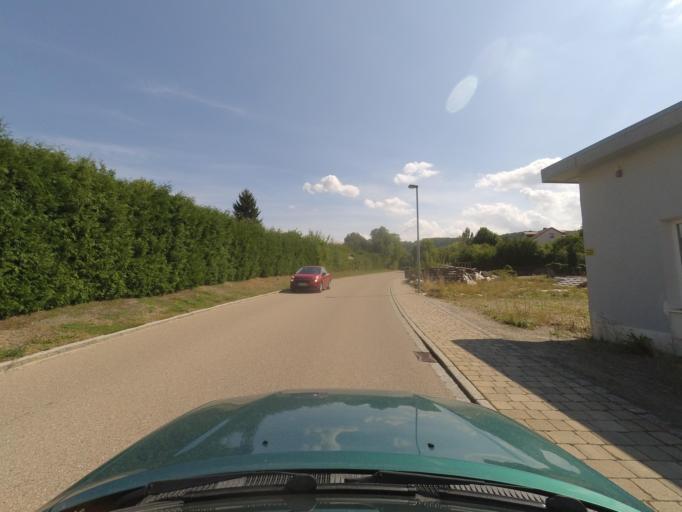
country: DE
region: Bavaria
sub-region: Regierungsbezirk Mittelfranken
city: Ettenstatt
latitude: 49.0771
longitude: 11.0575
